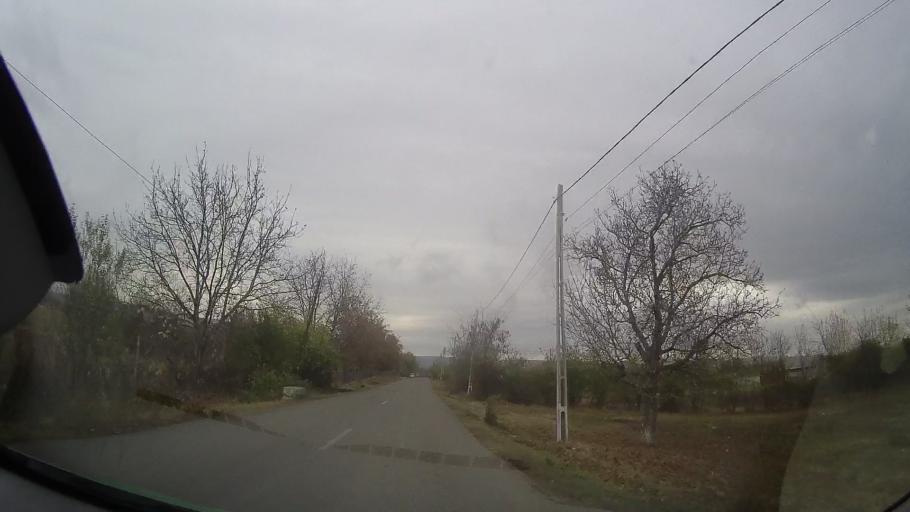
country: RO
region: Prahova
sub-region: Comuna Vadu Sapat
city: Vadu Sapat
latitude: 45.0286
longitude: 26.3840
